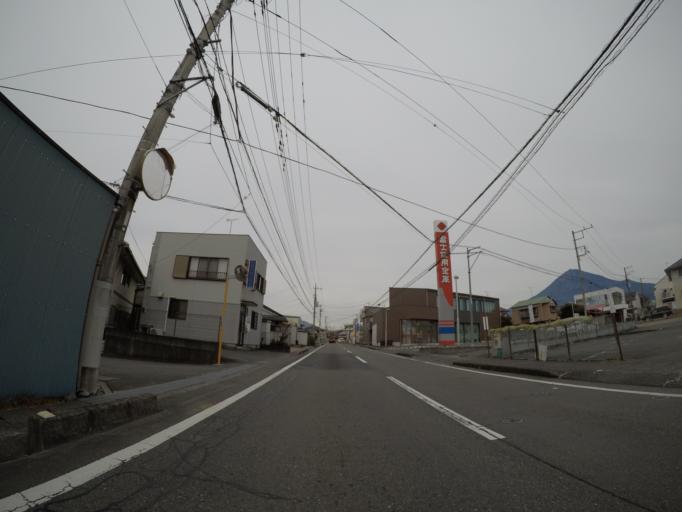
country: JP
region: Shizuoka
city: Fujinomiya
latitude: 35.2347
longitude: 138.6151
